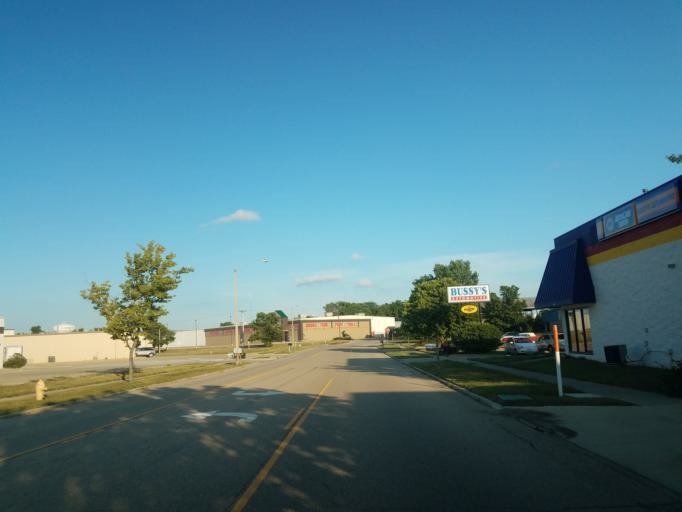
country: US
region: Illinois
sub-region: McLean County
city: Bloomington
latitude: 40.4551
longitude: -88.9736
